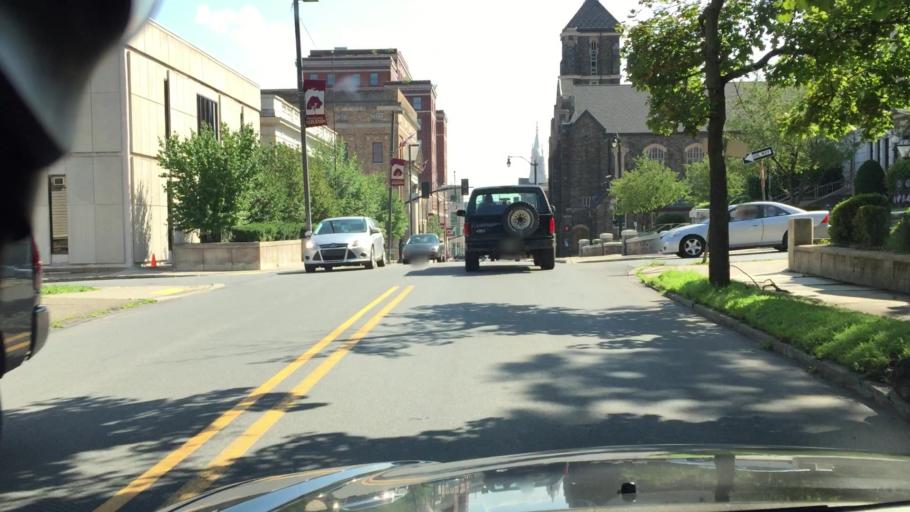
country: US
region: Pennsylvania
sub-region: Luzerne County
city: Hazleton
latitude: 40.9565
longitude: -75.9762
